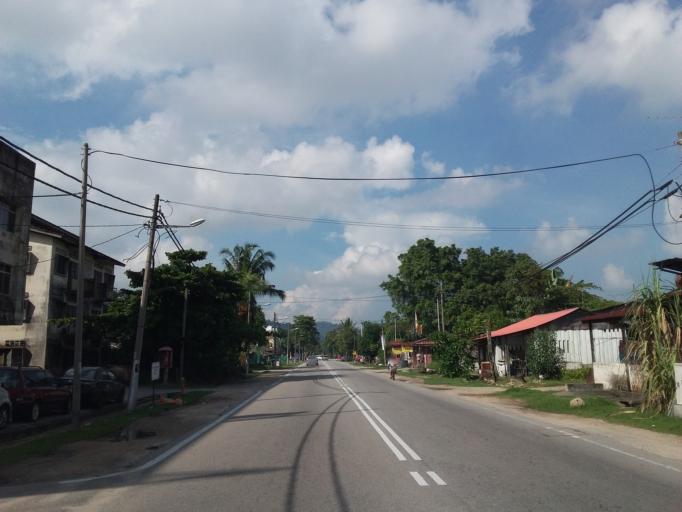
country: MY
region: Johor
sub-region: Daerah Batu Pahat
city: Batu Pahat
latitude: 1.8453
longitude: 102.9247
